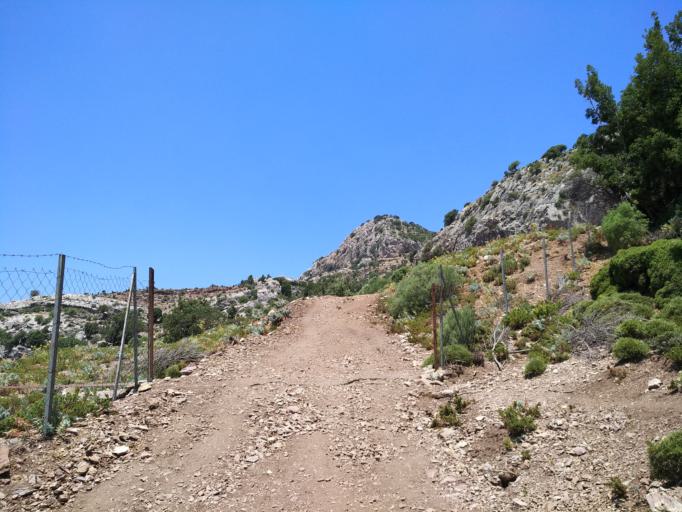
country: TR
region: Mugla
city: OEluedeniz
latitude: 36.5313
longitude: 29.1571
